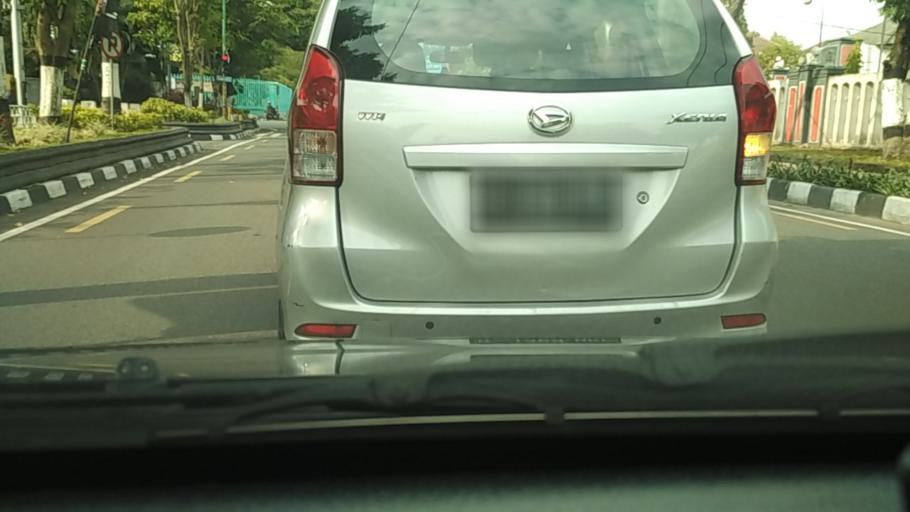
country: ID
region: Daerah Istimewa Yogyakarta
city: Yogyakarta
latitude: -7.7982
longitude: 110.3849
